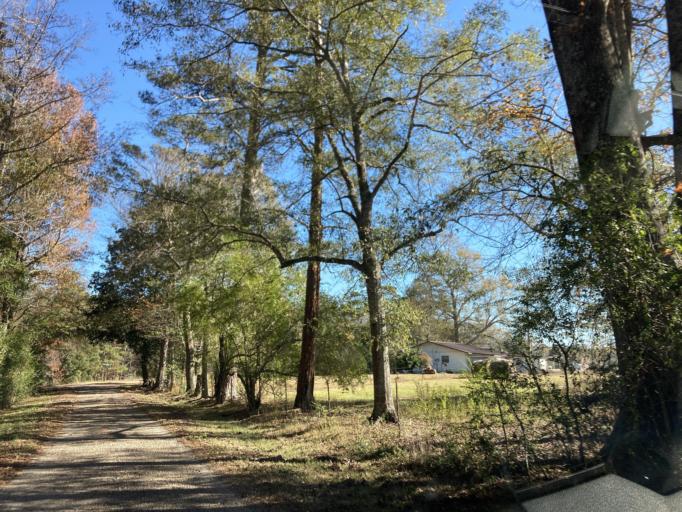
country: US
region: Mississippi
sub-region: Lamar County
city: Sumrall
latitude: 31.3102
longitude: -89.6520
